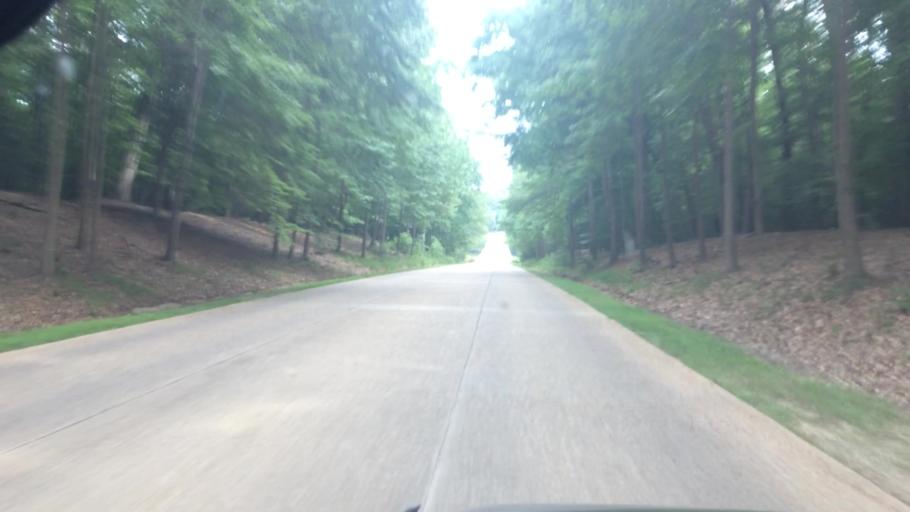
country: US
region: Virginia
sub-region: City of Williamsburg
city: Williamsburg
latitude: 37.2381
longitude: -76.6978
